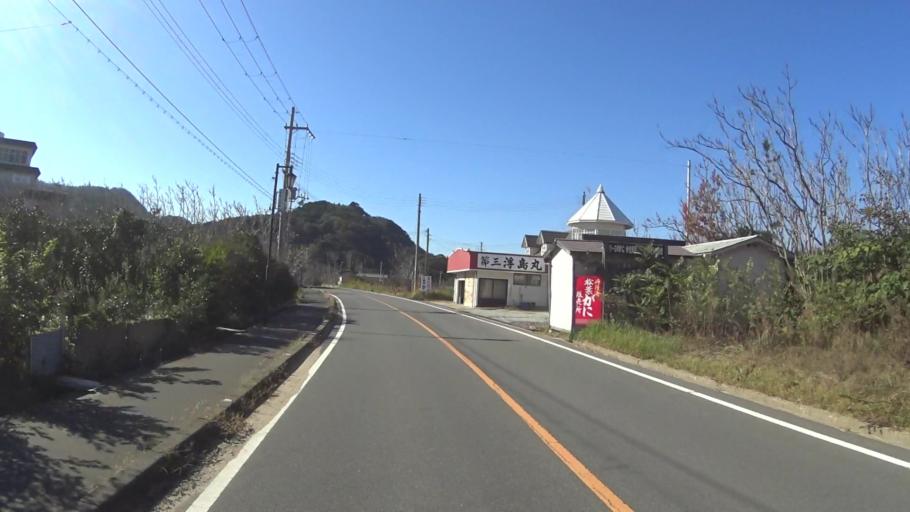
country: JP
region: Hyogo
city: Toyooka
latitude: 35.6447
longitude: 134.9056
